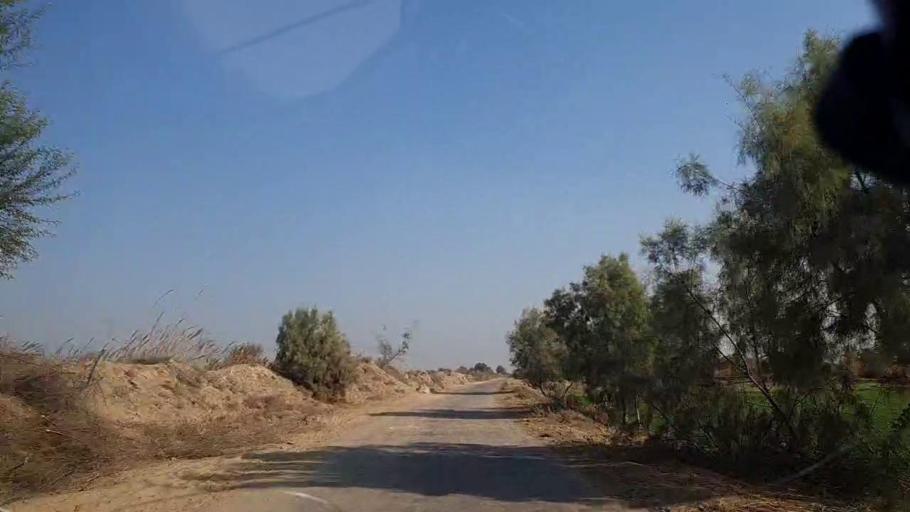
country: PK
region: Sindh
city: Khanpur
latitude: 27.6875
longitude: 69.5170
